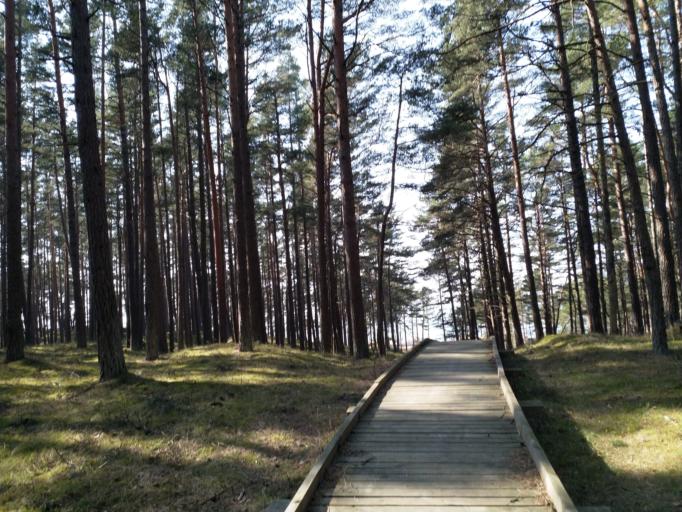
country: LV
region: Alsunga
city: Alsunga
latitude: 57.1595
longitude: 21.4104
